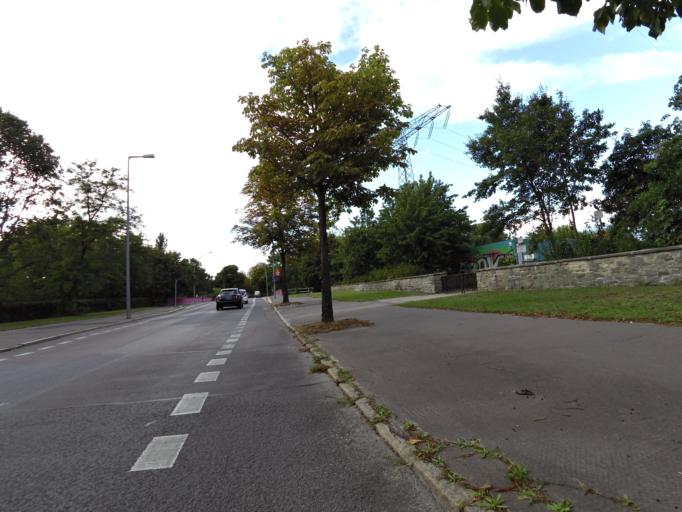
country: DE
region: Berlin
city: Baumschulenweg
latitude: 52.4620
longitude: 13.4923
